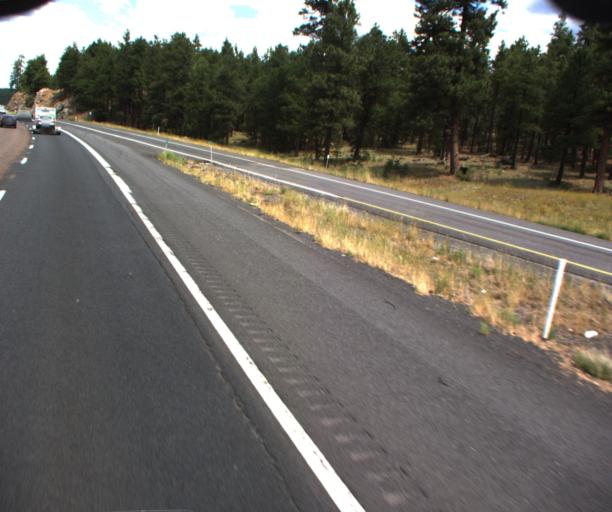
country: US
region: Arizona
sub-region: Coconino County
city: Mountainaire
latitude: 35.0542
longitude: -111.6827
